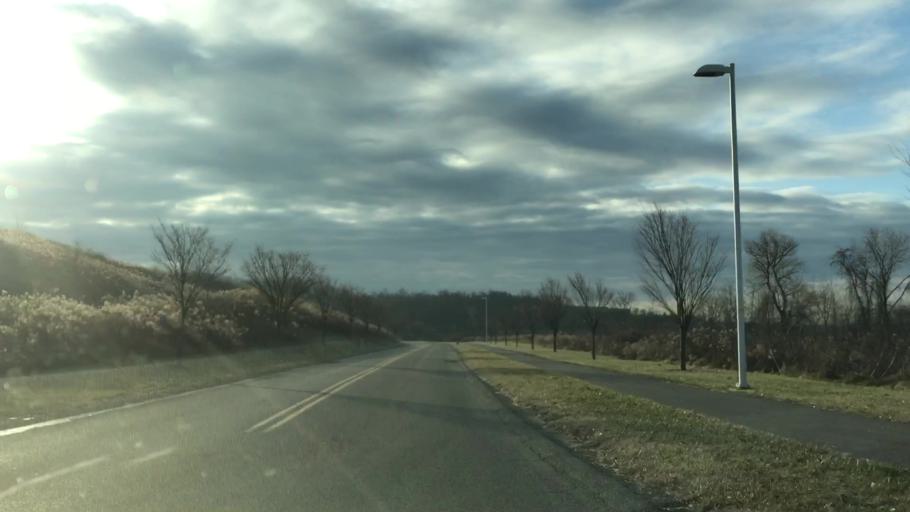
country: US
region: Pennsylvania
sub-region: Allegheny County
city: Carnot-Moon
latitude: 40.4890
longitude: -80.1963
